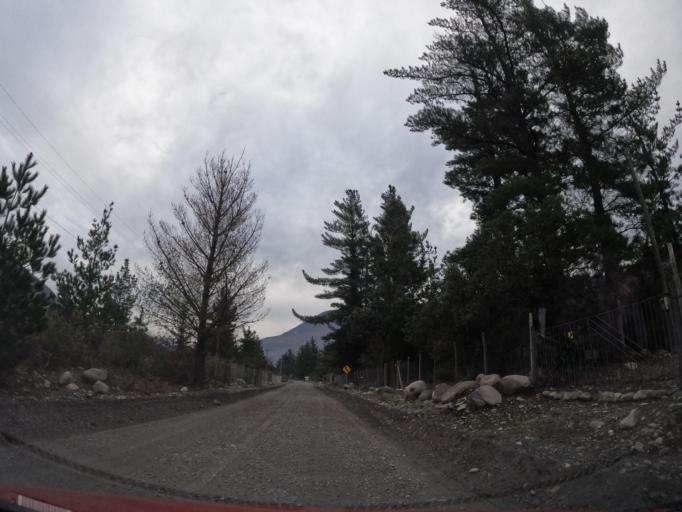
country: CL
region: Maule
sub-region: Provincia de Linares
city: Colbun
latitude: -35.7043
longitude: -71.0855
